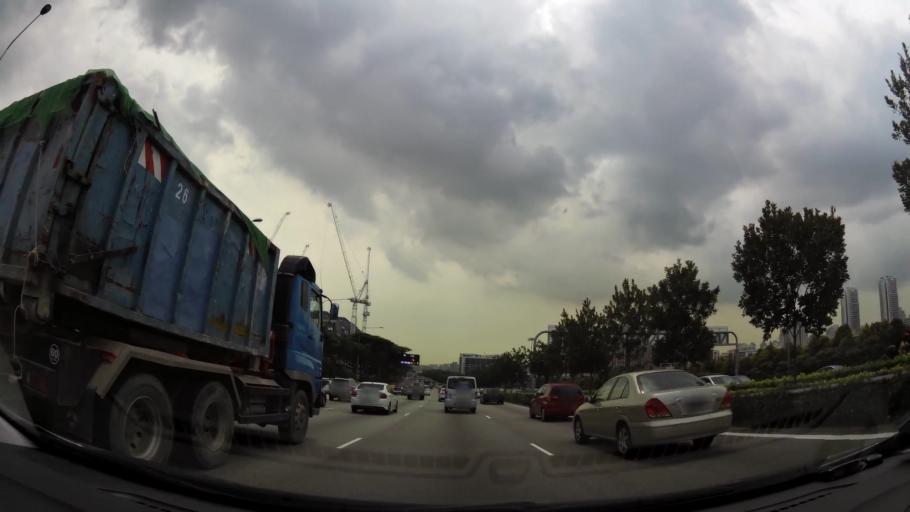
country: SG
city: Singapore
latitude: 1.3527
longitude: 103.8572
